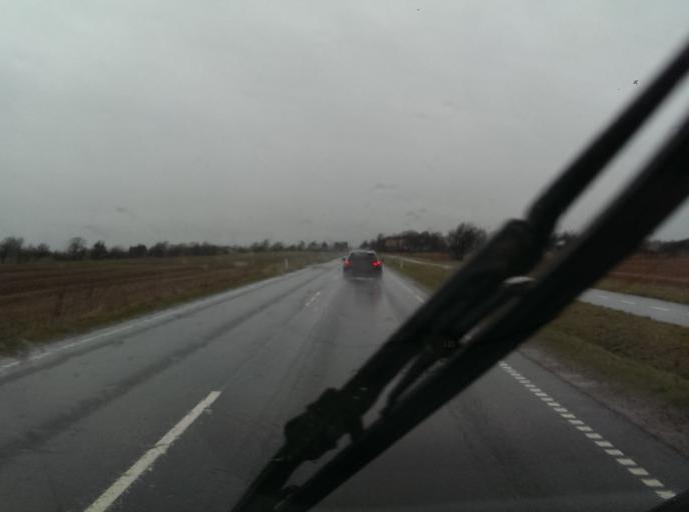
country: DK
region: South Denmark
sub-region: Varde Kommune
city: Olgod
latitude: 55.7428
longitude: 8.6186
